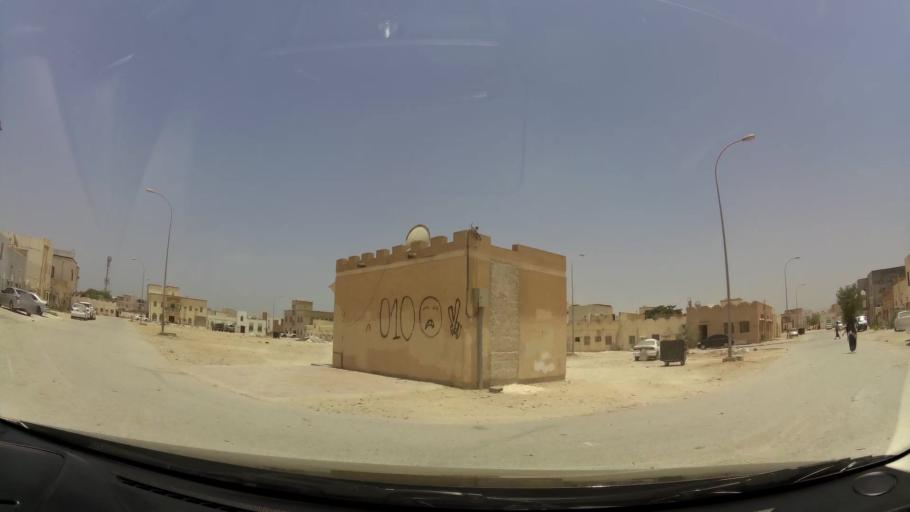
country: OM
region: Zufar
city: Salalah
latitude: 17.0807
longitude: 54.1533
